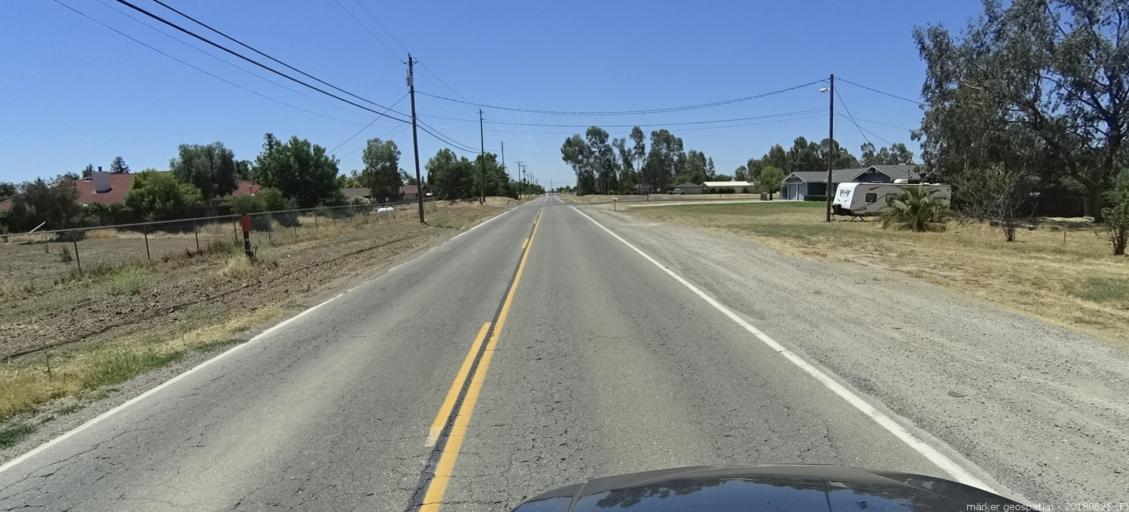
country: US
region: California
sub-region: Madera County
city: Bonadelle Ranchos-Madera Ranchos
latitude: 36.9336
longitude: -119.8942
